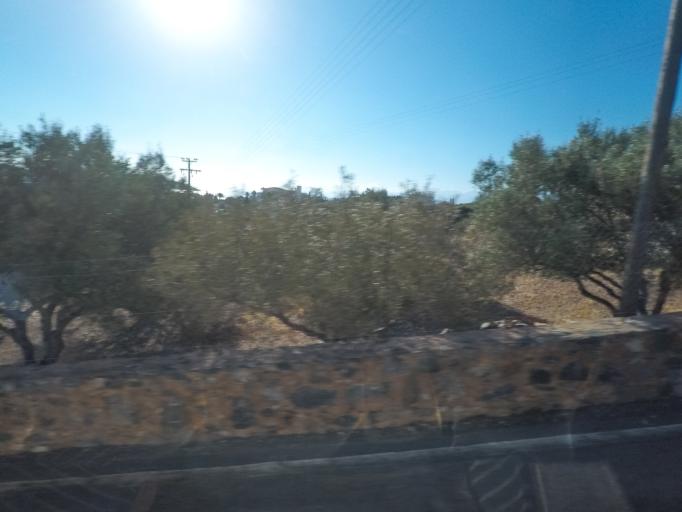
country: GR
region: Crete
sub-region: Nomos Lasithiou
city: Skhisma
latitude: 35.2465
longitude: 25.7267
